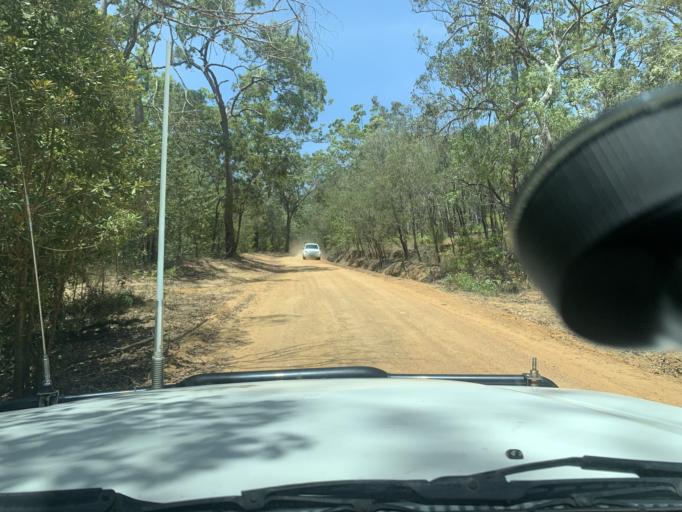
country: AU
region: Queensland
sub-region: Cairns
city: Redlynch
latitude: -16.9268
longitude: 145.6031
